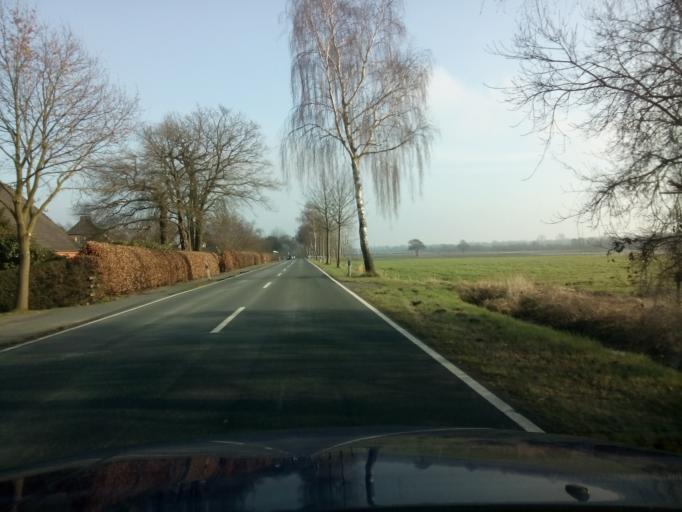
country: DE
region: Lower Saxony
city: Grasberg
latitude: 53.1266
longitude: 9.0338
